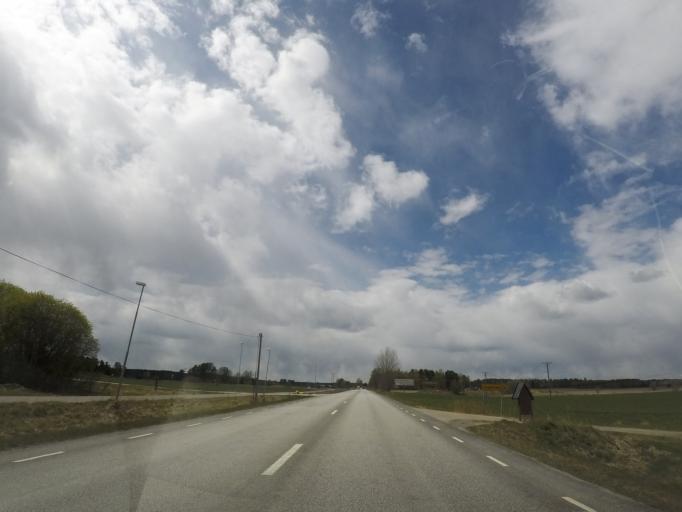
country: SE
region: Soedermanland
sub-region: Nykopings Kommun
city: Svalsta
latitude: 58.7429
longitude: 16.9016
